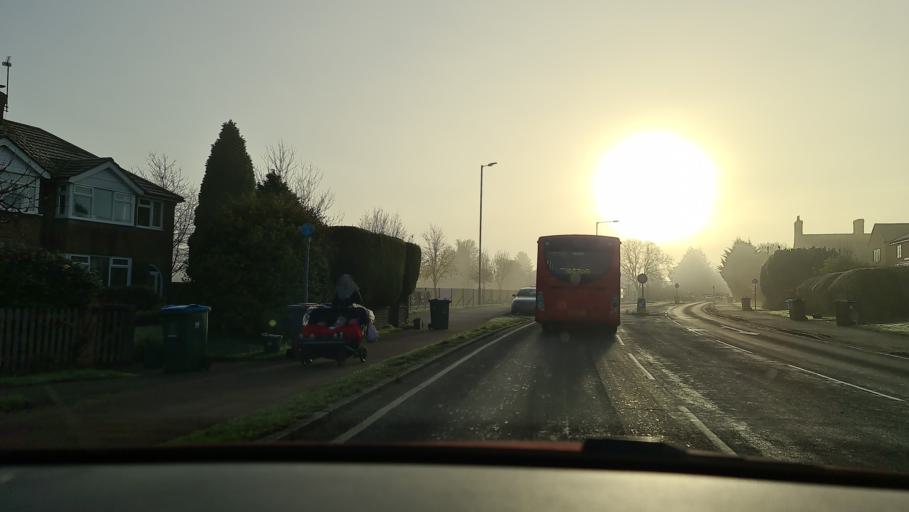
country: GB
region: England
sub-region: Buckinghamshire
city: Wendover
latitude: 51.7719
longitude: -0.7488
